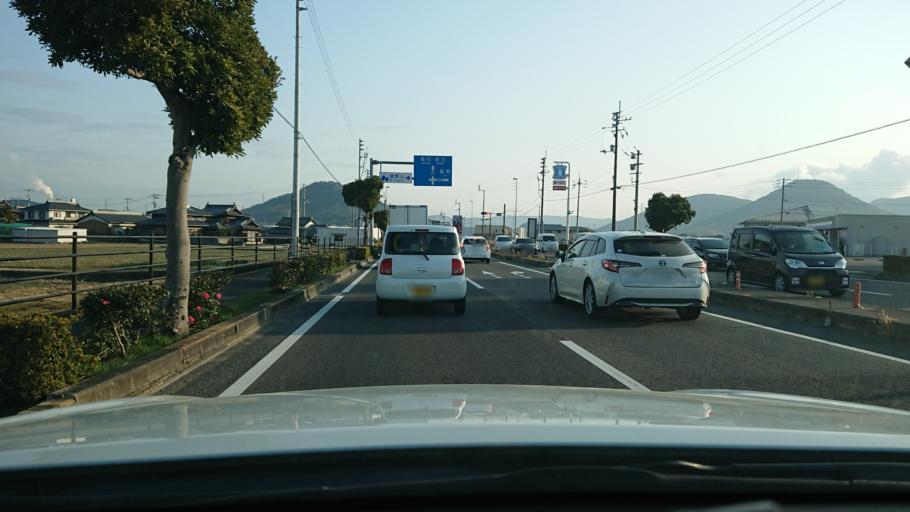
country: JP
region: Kagawa
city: Sakaidecho
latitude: 34.2874
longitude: 133.8288
